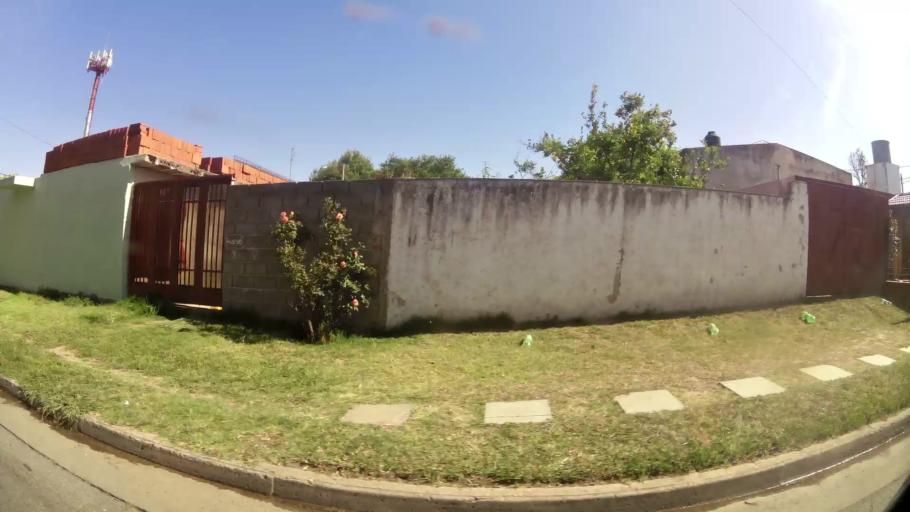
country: AR
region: Cordoba
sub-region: Departamento de Capital
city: Cordoba
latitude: -31.3608
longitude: -64.1687
